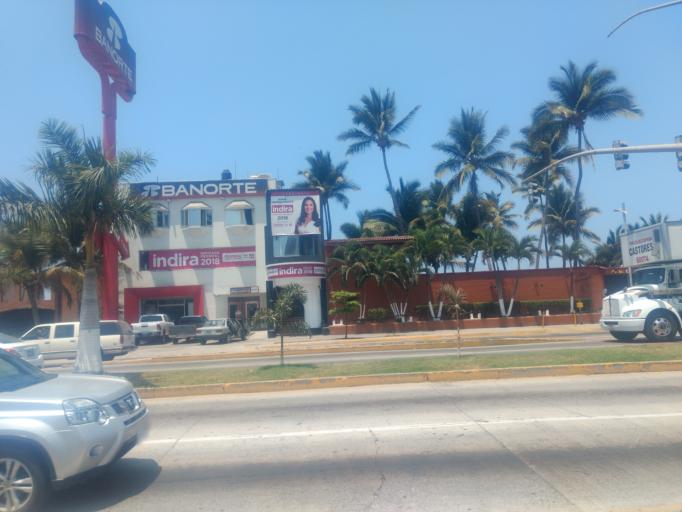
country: MX
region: Colima
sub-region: Manzanillo
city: Manzanillo
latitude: 19.0951
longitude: -104.3189
